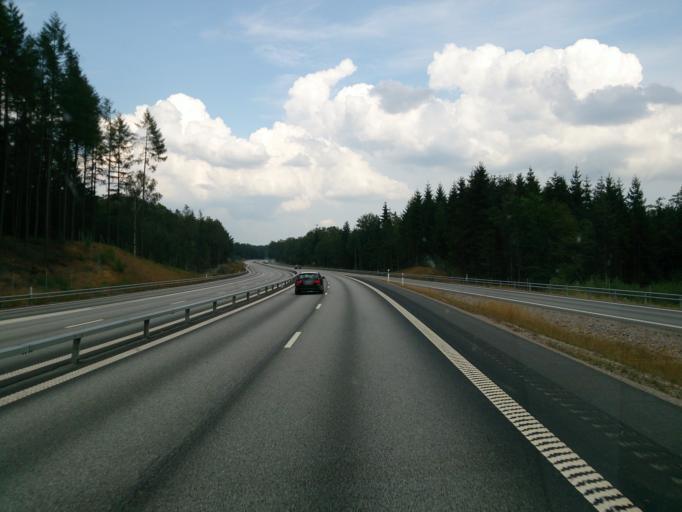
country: SE
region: Skane
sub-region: Horby Kommun
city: Hoerby
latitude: 55.9048
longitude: 13.7404
